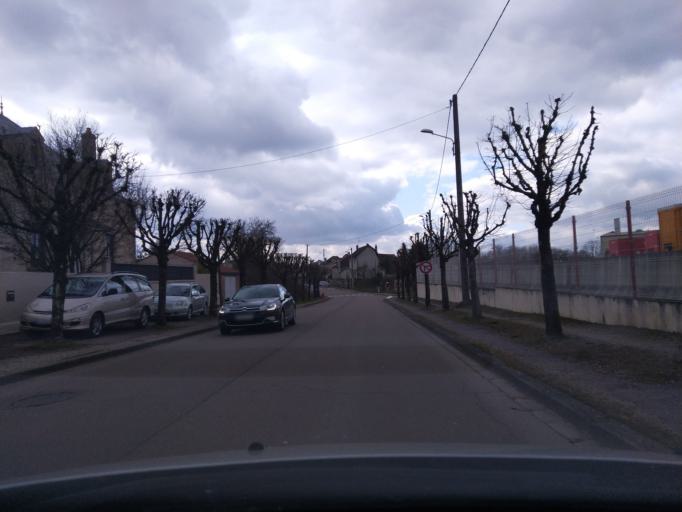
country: FR
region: Bourgogne
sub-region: Departement de l'Yonne
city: Avallon
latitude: 47.4937
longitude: 3.9211
